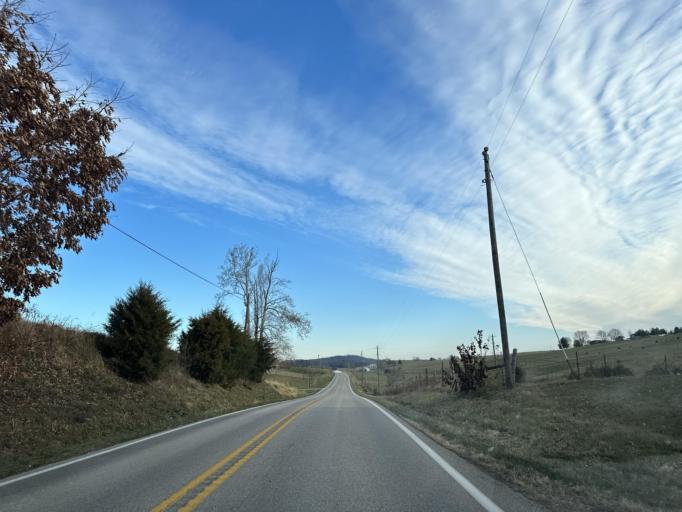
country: US
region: Virginia
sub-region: Rockingham County
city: Bridgewater
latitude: 38.3477
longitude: -79.0352
